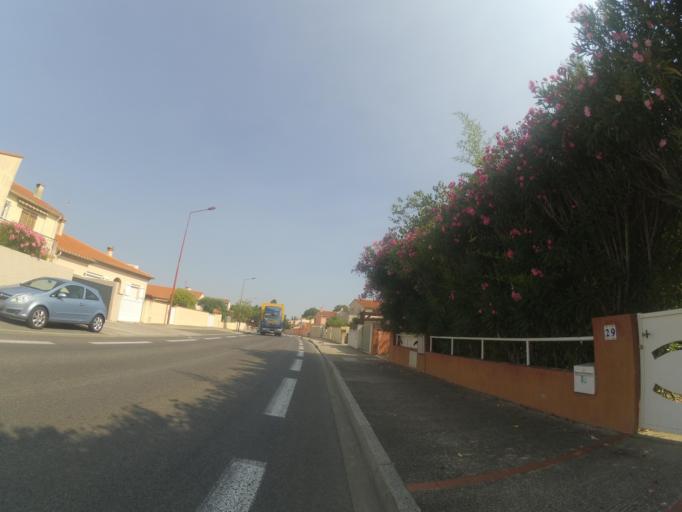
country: FR
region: Languedoc-Roussillon
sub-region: Departement des Pyrenees-Orientales
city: Toulouges
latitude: 42.6695
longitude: 2.8353
